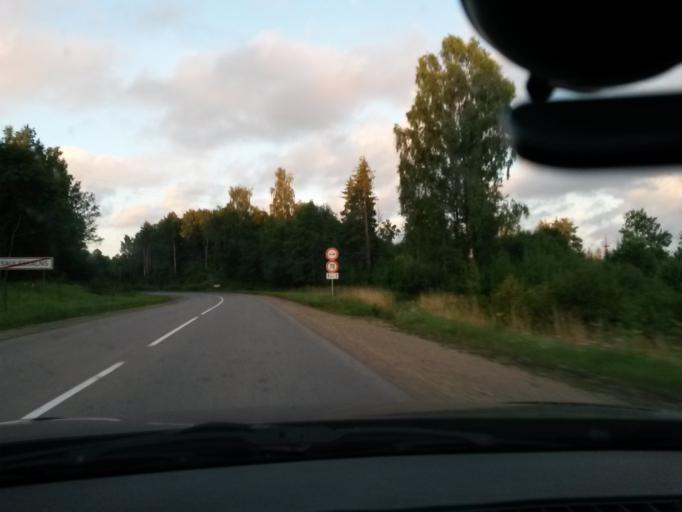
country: LV
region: Madonas Rajons
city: Madona
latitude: 56.8050
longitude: 26.0805
